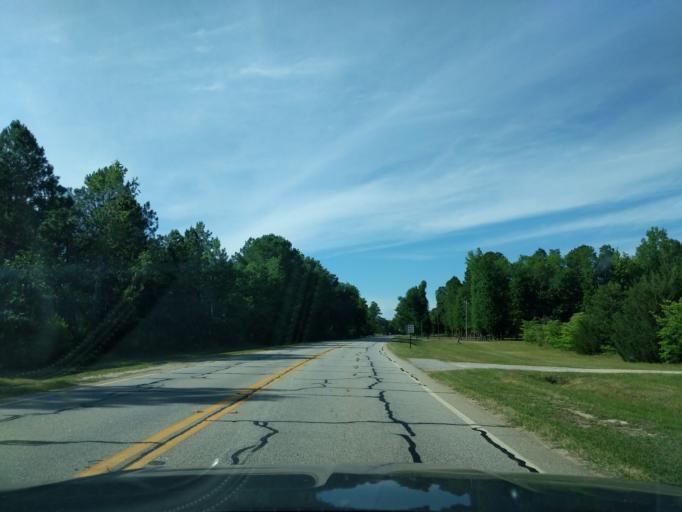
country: US
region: Georgia
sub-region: Jefferson County
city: Wrens
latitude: 33.2474
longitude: -82.3873
